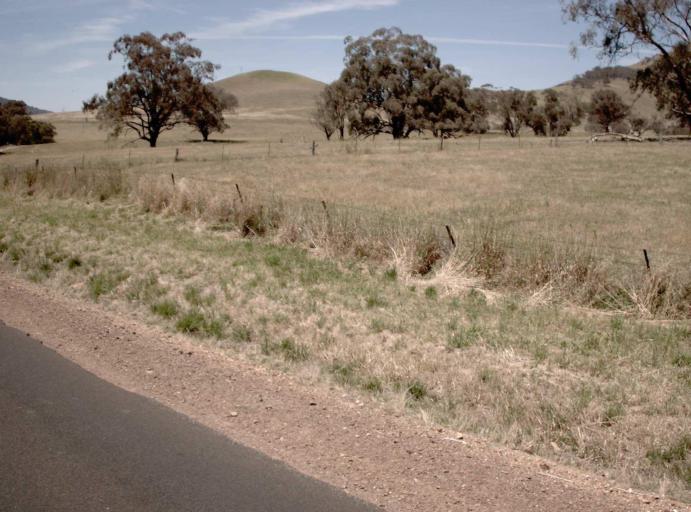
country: AU
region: Victoria
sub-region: East Gippsland
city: Bairnsdale
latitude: -37.1780
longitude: 147.7048
